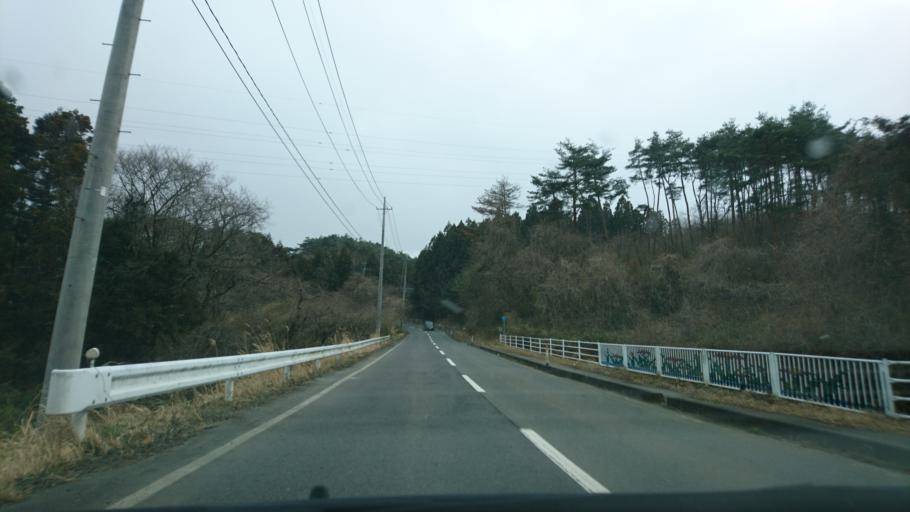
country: JP
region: Iwate
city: Ichinoseki
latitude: 38.8329
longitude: 141.1714
